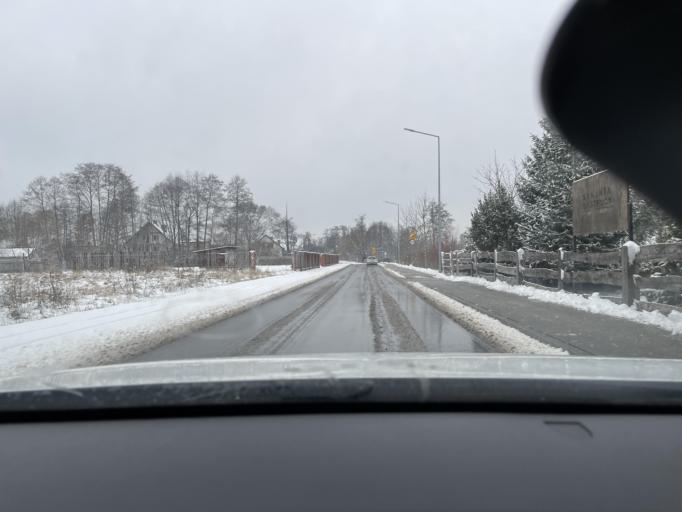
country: PL
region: Masovian Voivodeship
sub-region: Powiat zyrardowski
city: Zyrardow
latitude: 52.0417
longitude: 20.4467
